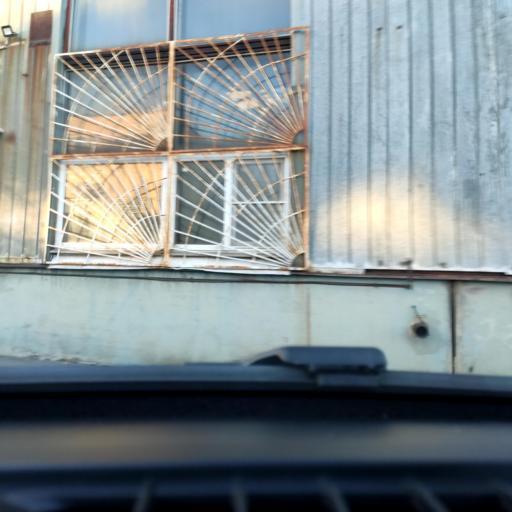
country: RU
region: Voronezj
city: Somovo
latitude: 51.6740
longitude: 39.2952
